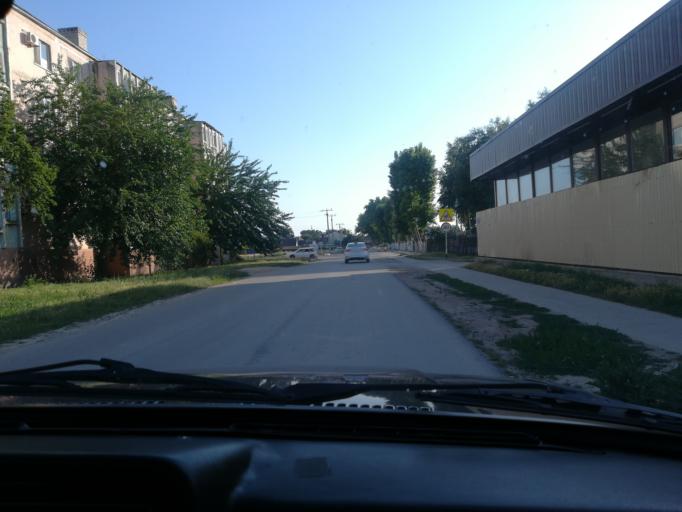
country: RU
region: Krasnodarskiy
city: Vityazevo
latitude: 45.0049
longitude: 37.2897
